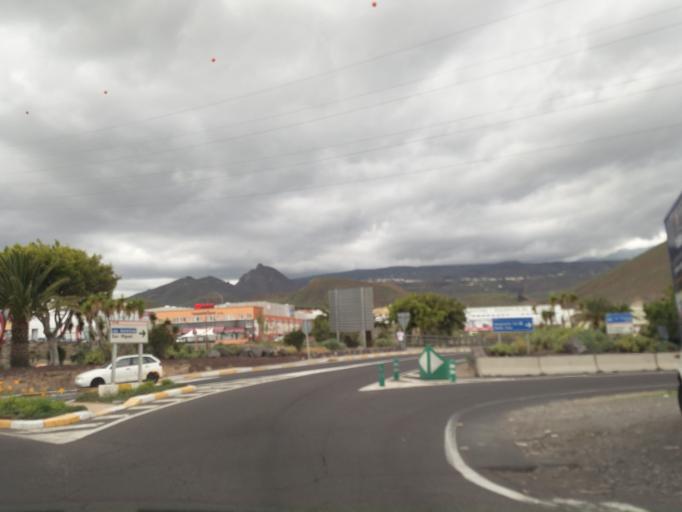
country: ES
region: Canary Islands
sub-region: Provincia de Santa Cruz de Tenerife
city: San Miguel
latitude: 28.0510
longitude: -16.6118
